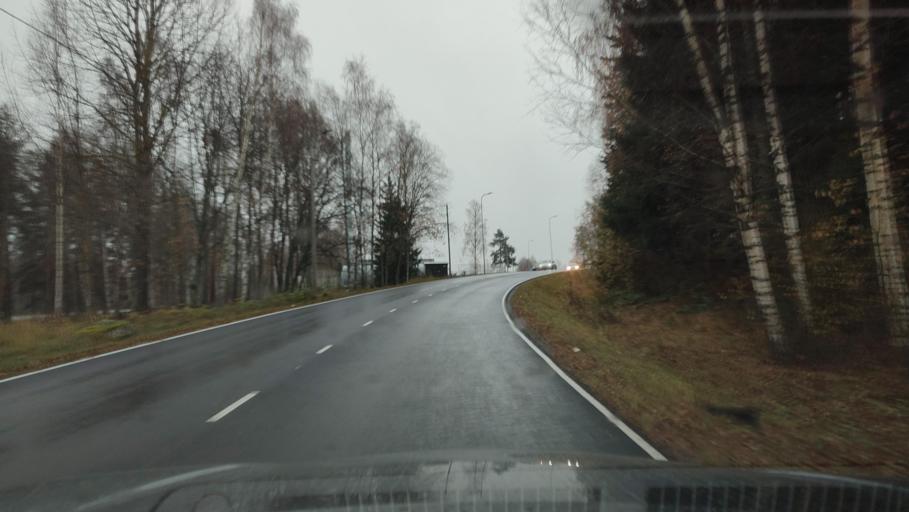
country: FI
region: Ostrobothnia
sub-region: Vaasa
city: Vaasa
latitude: 63.0978
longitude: 21.6503
